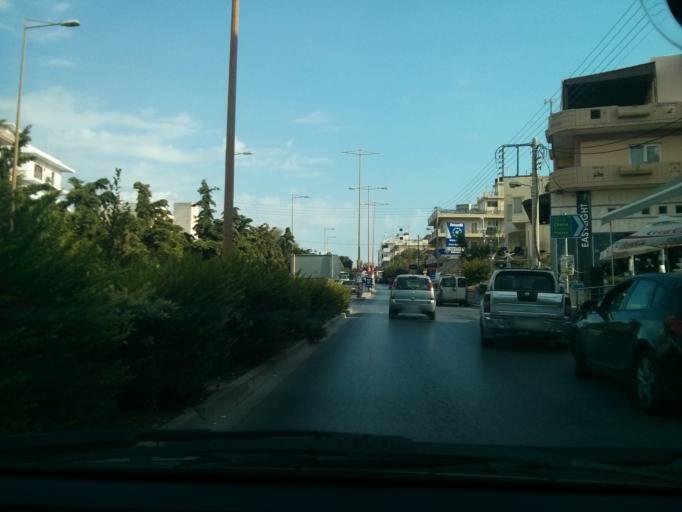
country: GR
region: Crete
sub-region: Nomos Irakleiou
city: Irakleion
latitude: 35.3248
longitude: 25.1397
